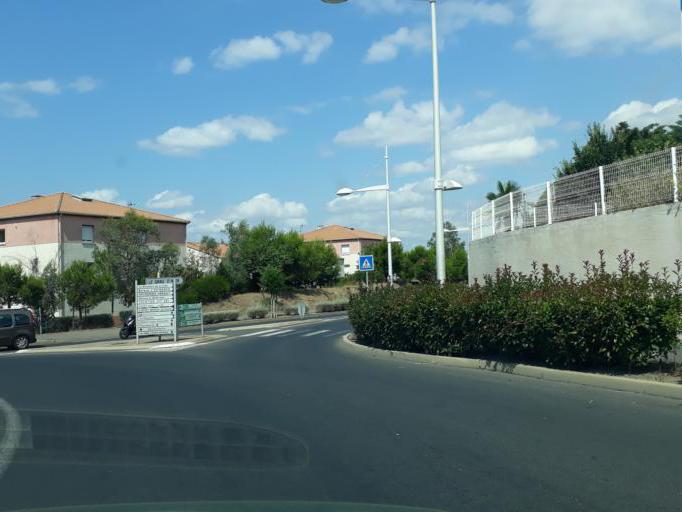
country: FR
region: Languedoc-Roussillon
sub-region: Departement de l'Herault
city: Agde
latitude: 43.3006
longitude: 3.4721
